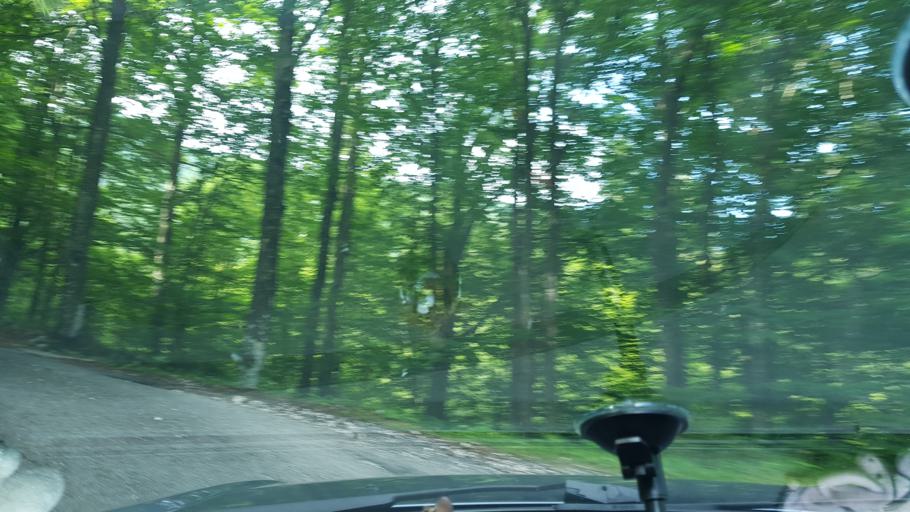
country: IT
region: Friuli Venezia Giulia
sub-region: Provincia di Udine
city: Prato
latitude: 46.3394
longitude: 13.4104
